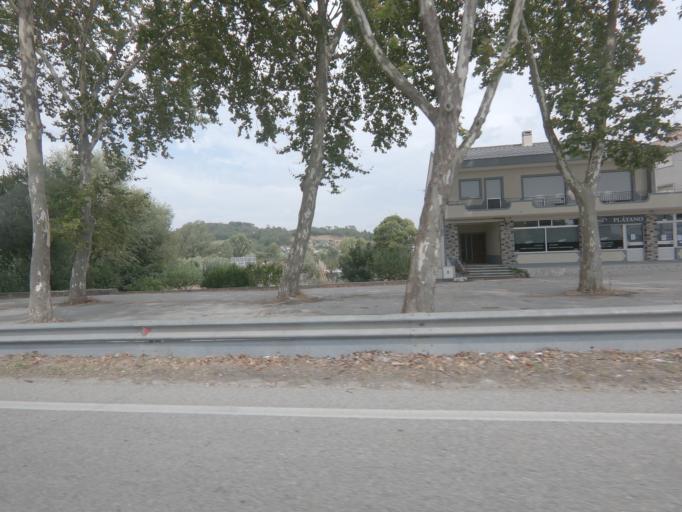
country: PT
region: Leiria
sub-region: Pombal
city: Pombal
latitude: 39.9051
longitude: -8.6338
